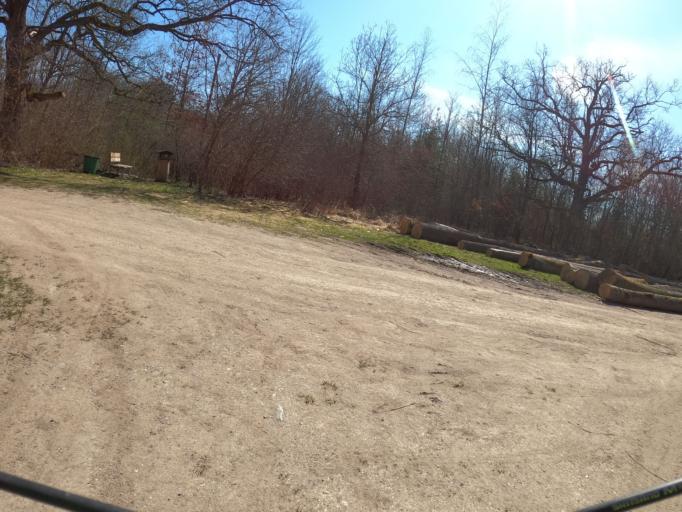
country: DE
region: Bavaria
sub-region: Swabia
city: Nersingen
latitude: 48.4406
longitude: 10.1348
